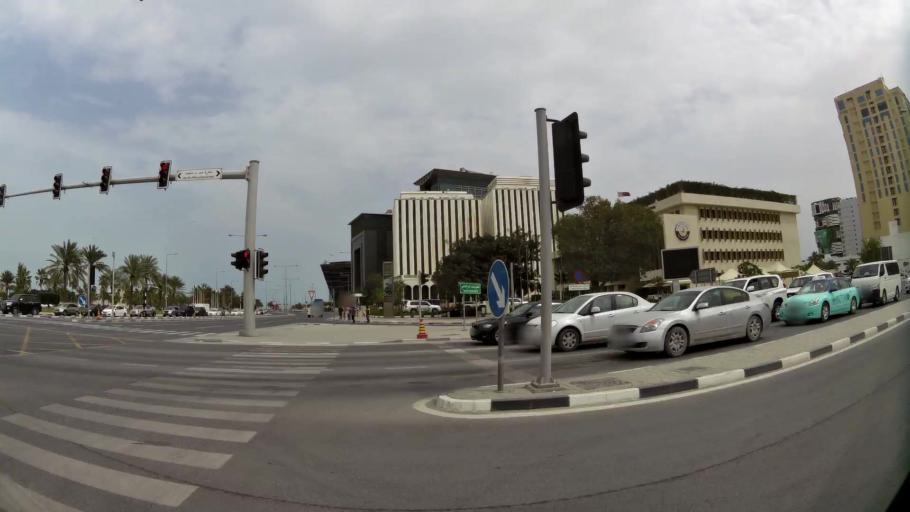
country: QA
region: Baladiyat ad Dawhah
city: Doha
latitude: 25.2907
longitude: 51.5392
